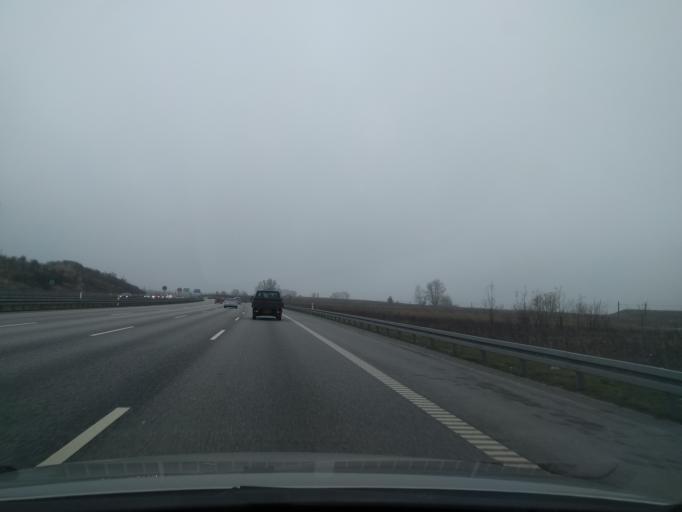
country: DK
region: Zealand
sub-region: Solrod Kommune
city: Solrod Strand
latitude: 55.5493
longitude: 12.2186
